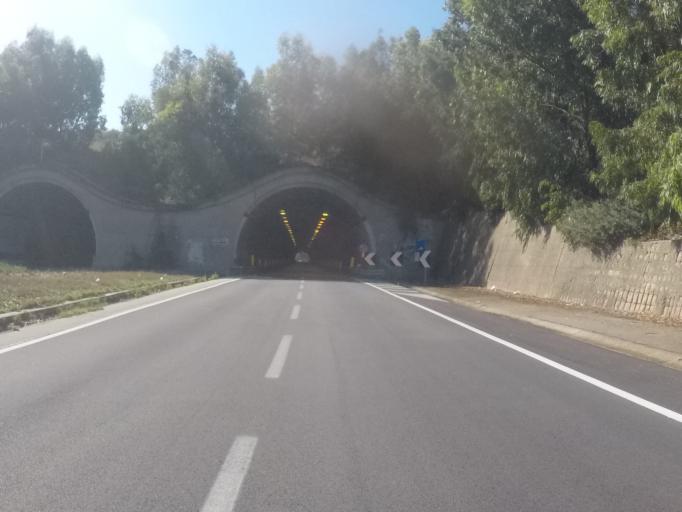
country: IT
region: Sicily
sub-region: Agrigento
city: Ribera
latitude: 37.4743
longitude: 13.2265
